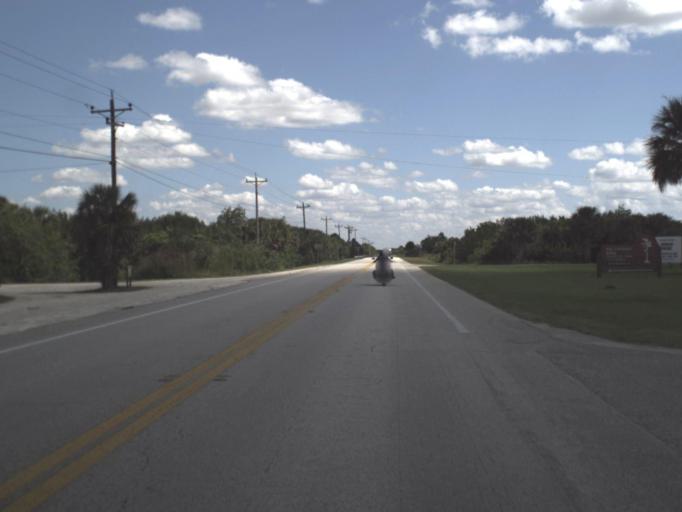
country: US
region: Florida
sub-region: Collier County
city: Marco
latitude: 25.9418
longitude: -81.4701
